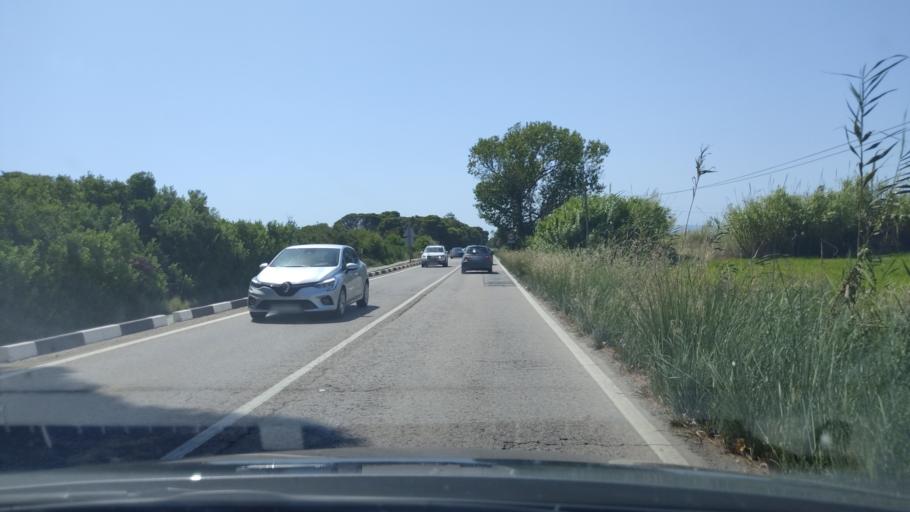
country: ES
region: Valencia
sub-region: Provincia de Valencia
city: Alfafar
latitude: 39.3746
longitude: -0.3311
